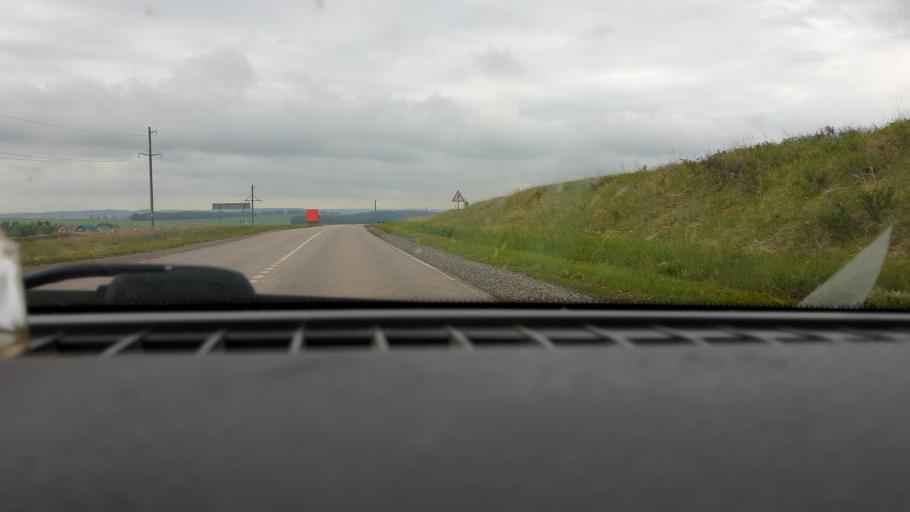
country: RU
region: Bashkortostan
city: Priyutovo
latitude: 53.9567
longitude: 53.9752
